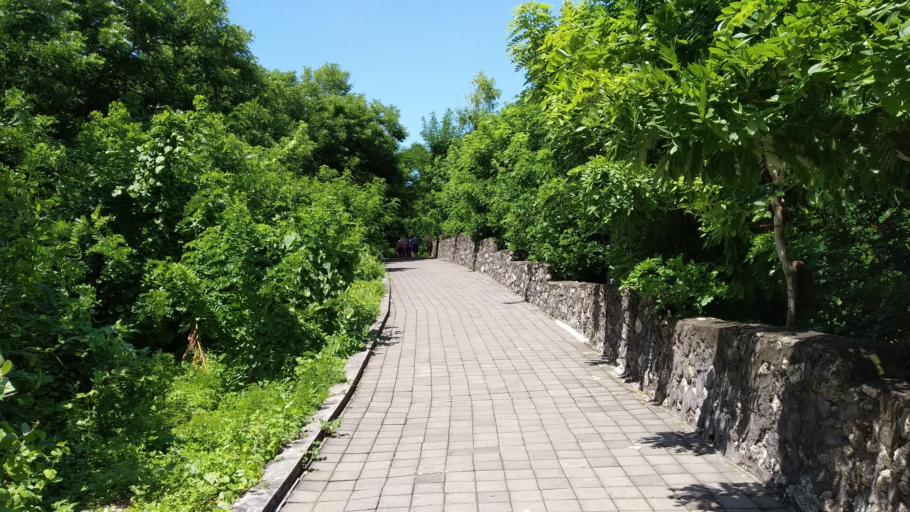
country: ID
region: Bali
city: Pecatu
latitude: -8.8314
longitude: 115.0863
